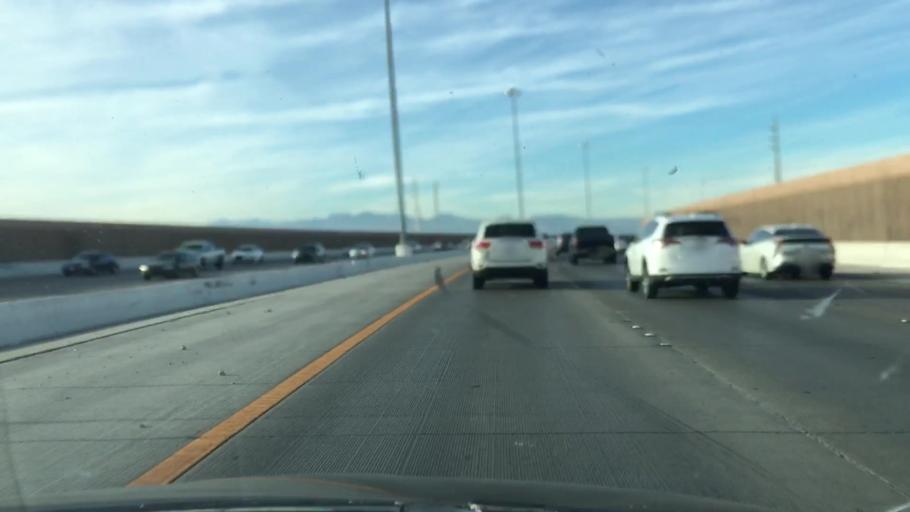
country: US
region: Nevada
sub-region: Clark County
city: Whitney
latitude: 36.0264
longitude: -115.1283
